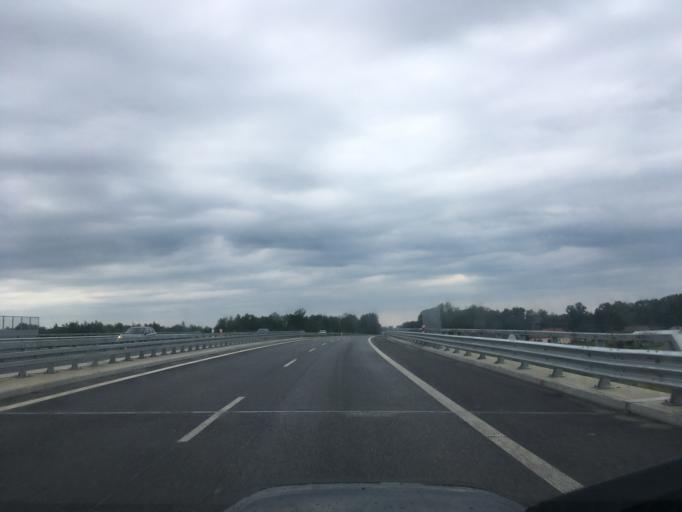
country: PL
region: Masovian Voivodeship
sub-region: Powiat piaseczynski
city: Gora Kalwaria
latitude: 51.9853
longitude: 21.1734
